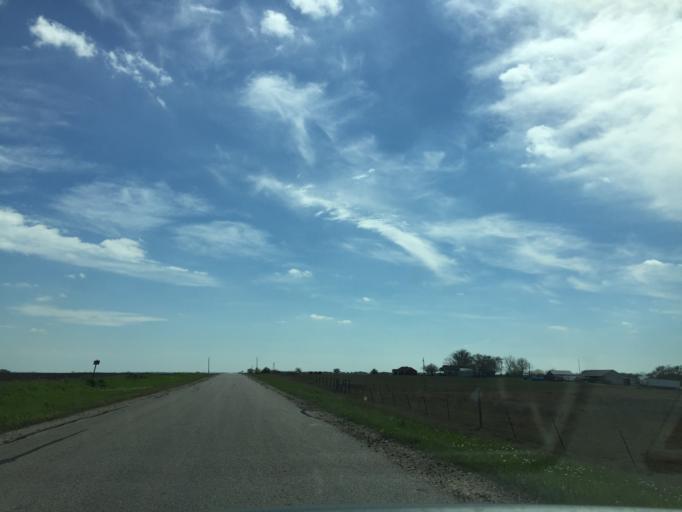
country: US
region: Texas
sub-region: Milam County
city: Thorndale
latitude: 30.5514
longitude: -97.2976
